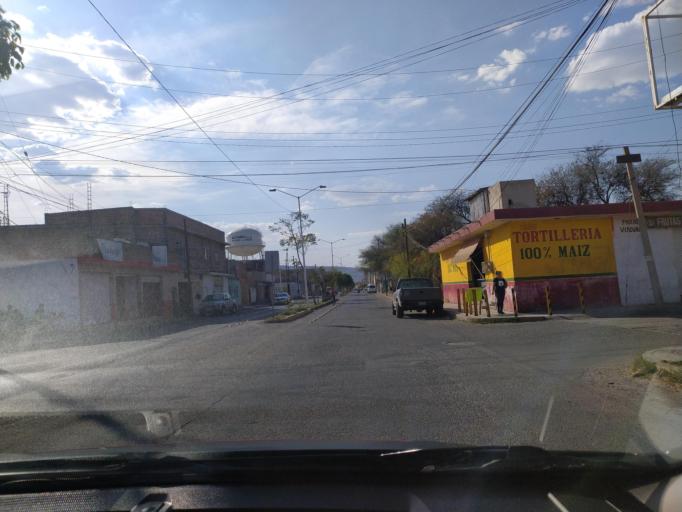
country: MX
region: Guanajuato
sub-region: San Francisco del Rincon
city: Fraccionamiento la Mezquitera
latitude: 21.0129
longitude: -101.8416
